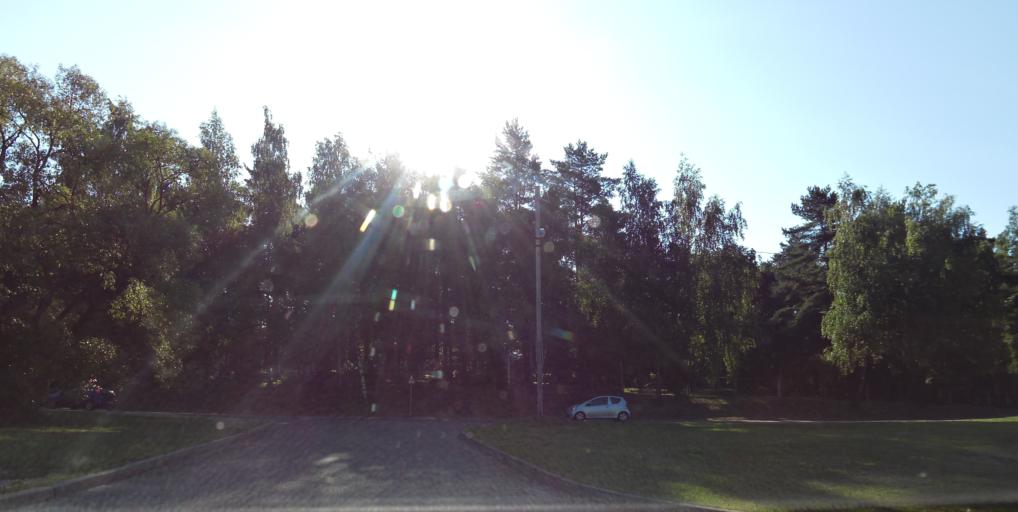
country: LT
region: Vilnius County
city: Seskine
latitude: 54.7083
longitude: 25.2378
